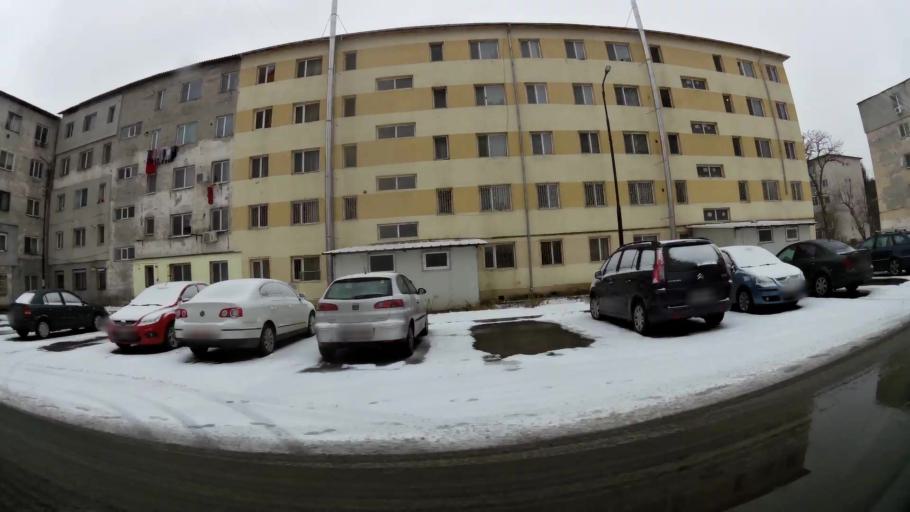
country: RO
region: Dambovita
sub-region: Municipiul Targoviste
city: Targoviste
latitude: 44.9207
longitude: 25.4741
